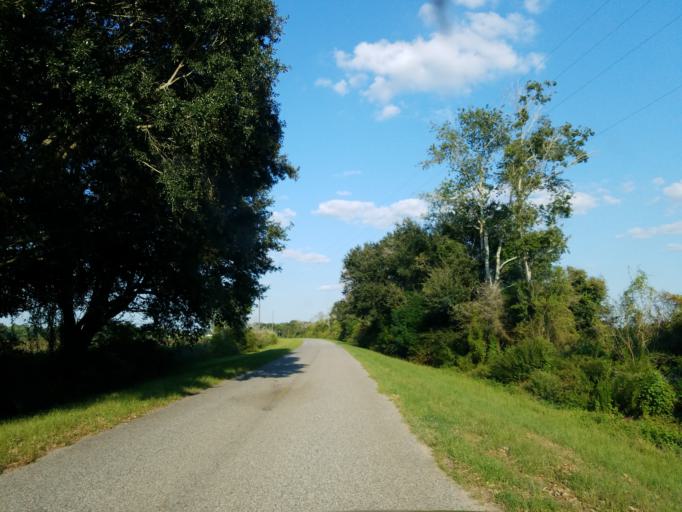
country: US
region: Georgia
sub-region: Cook County
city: Sparks
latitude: 31.2362
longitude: -83.4880
